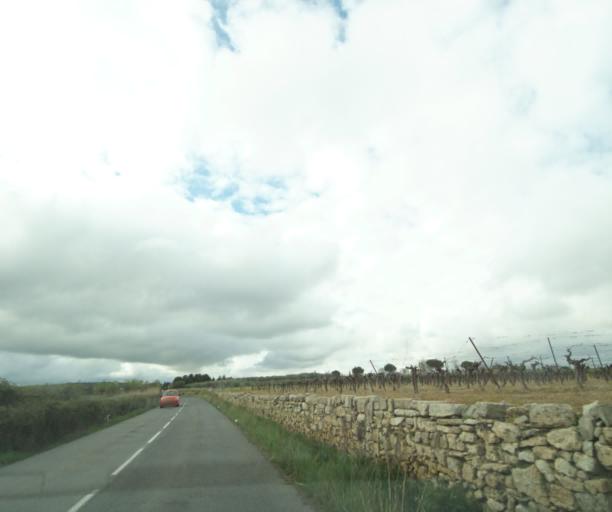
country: FR
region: Languedoc-Roussillon
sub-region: Departement de l'Herault
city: Saussan
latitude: 43.5768
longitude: 3.7702
